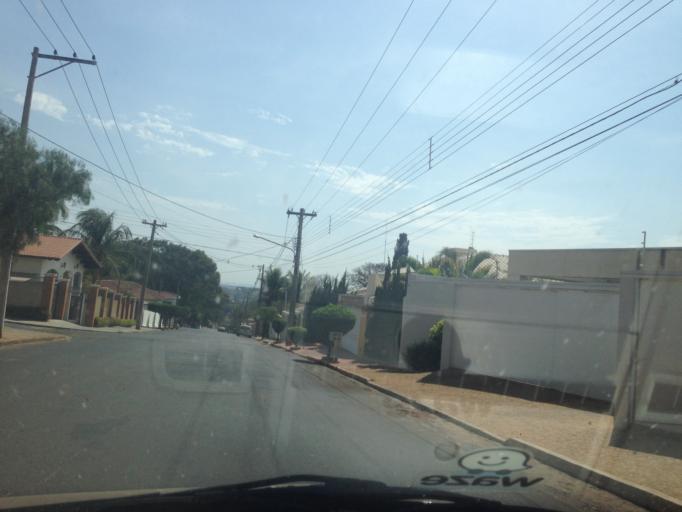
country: BR
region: Sao Paulo
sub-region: Casa Branca
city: Casa Branca
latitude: -21.7766
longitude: -47.0765
